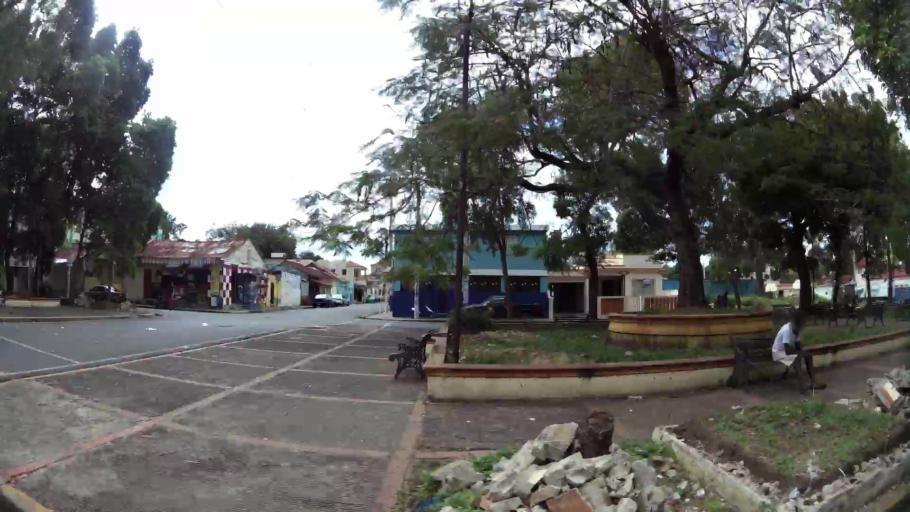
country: DO
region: Santiago
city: Santiago de los Caballeros
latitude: 19.4567
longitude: -70.7136
